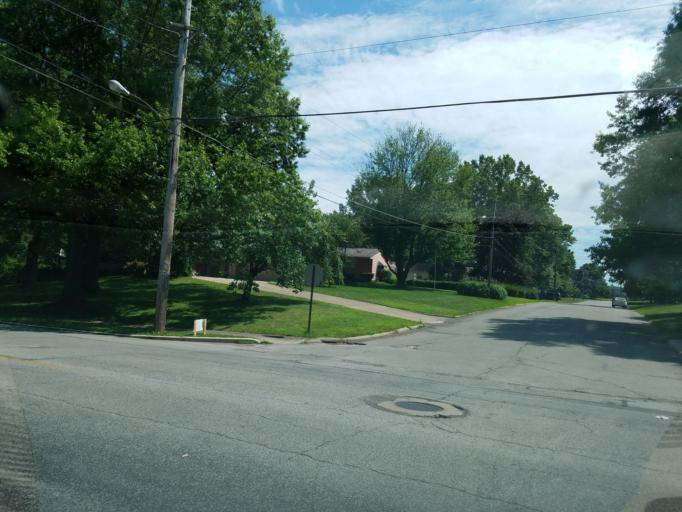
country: US
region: Ohio
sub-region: Ashland County
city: Ashland
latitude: 40.8582
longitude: -82.3361
